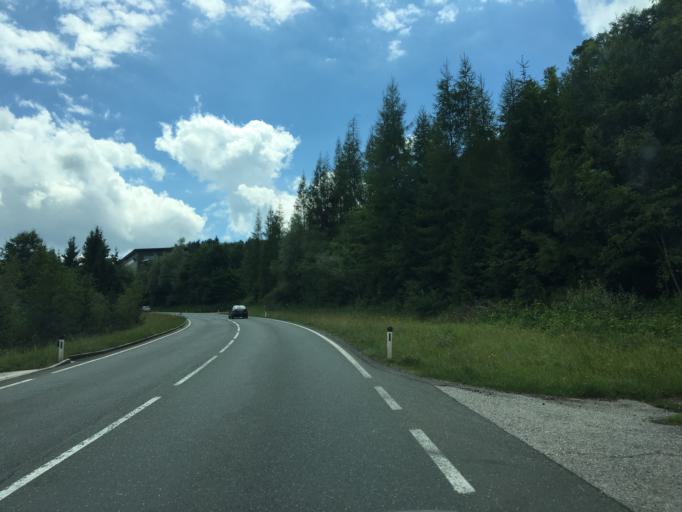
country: AT
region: Salzburg
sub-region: Politischer Bezirk Salzburg-Umgebung
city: Plainfeld
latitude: 47.8366
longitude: 13.1988
